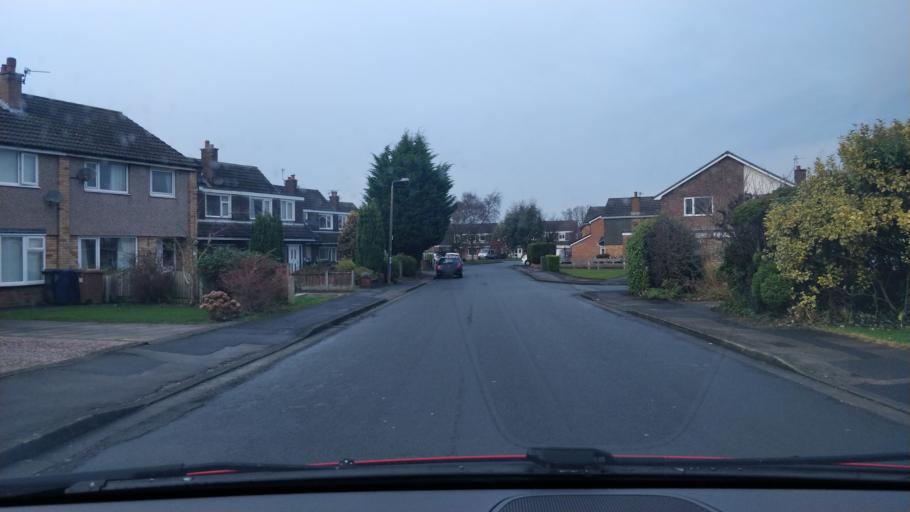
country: GB
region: England
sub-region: Lancashire
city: Preston
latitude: 53.7418
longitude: -2.7352
